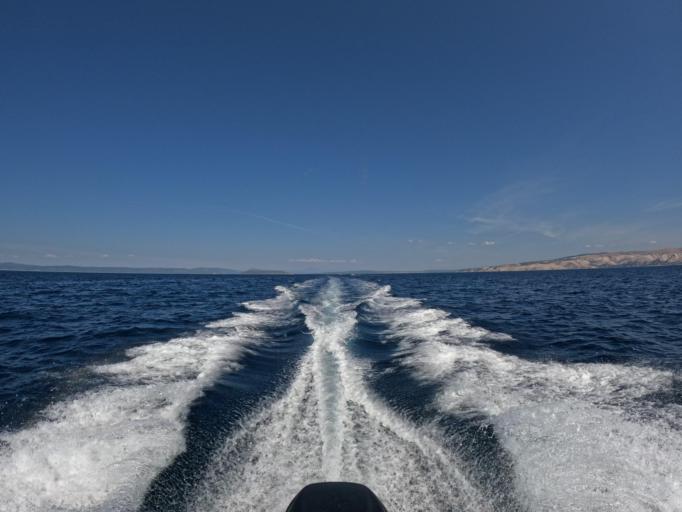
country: HR
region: Primorsko-Goranska
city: Lopar
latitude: 44.8913
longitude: 14.6444
